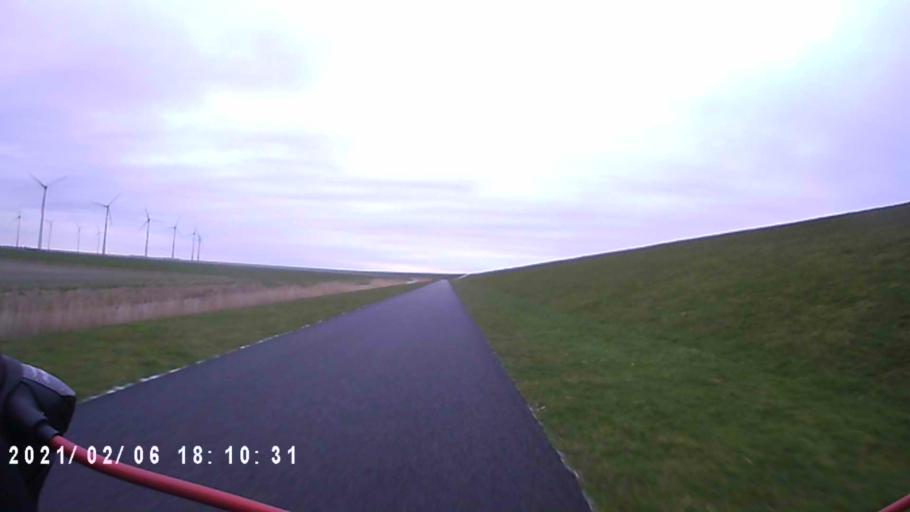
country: NL
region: Groningen
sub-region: Gemeente Appingedam
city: Appingedam
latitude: 53.4573
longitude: 6.7871
